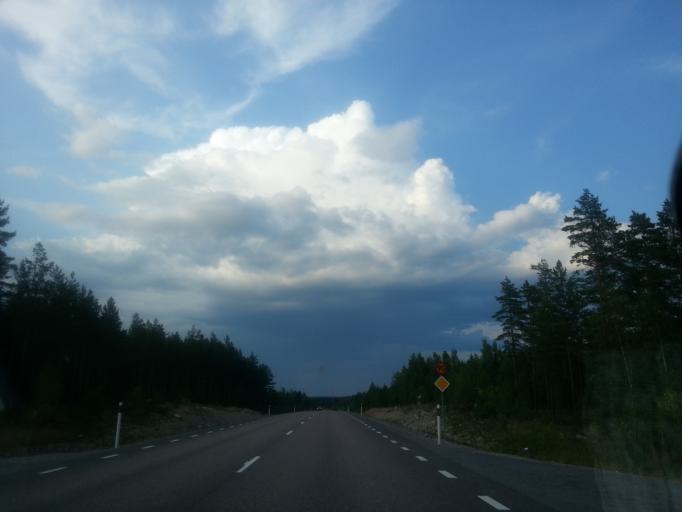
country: SE
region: Dalarna
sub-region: Avesta Kommun
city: Horndal
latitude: 60.3748
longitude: 16.4430
